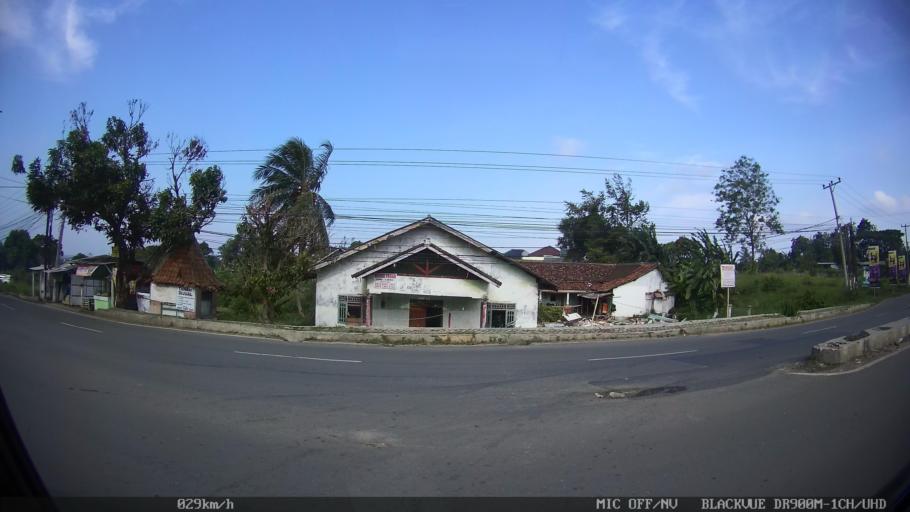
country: ID
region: Lampung
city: Kedaton
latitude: -5.3813
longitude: 105.2215
